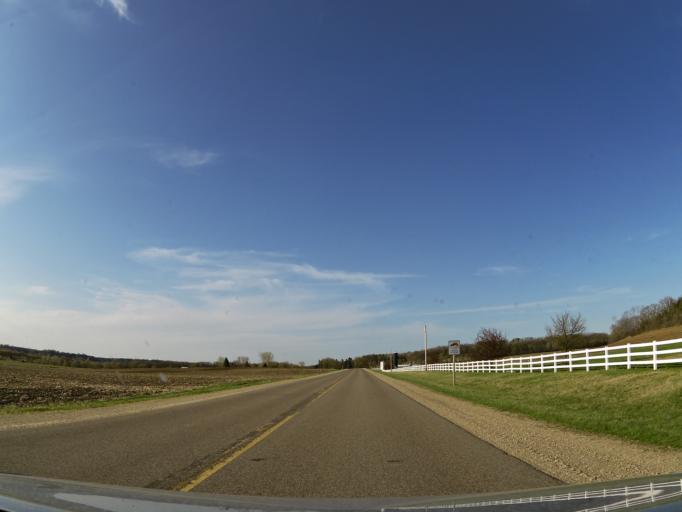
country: US
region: Wisconsin
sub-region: Pierce County
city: River Falls
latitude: 44.7970
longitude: -92.6455
